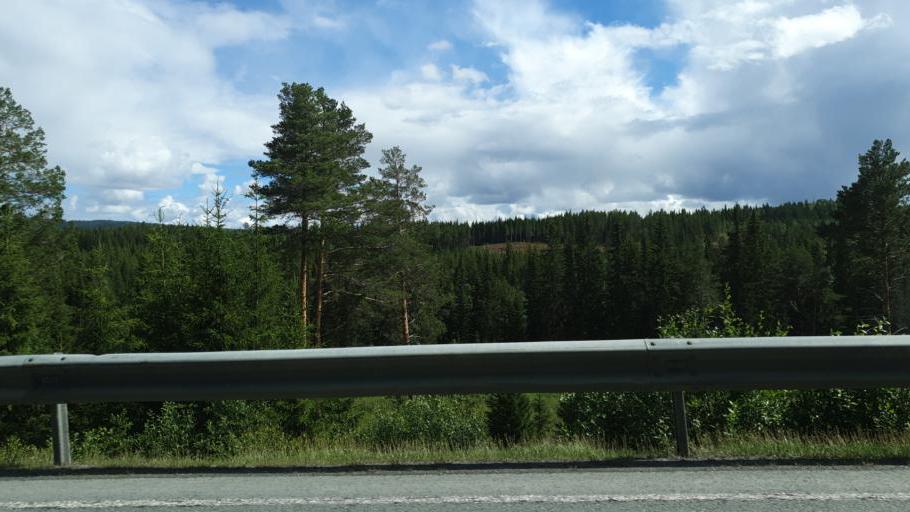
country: NO
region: Sor-Trondelag
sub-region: Rennebu
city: Berkak
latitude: 62.7136
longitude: 9.9601
